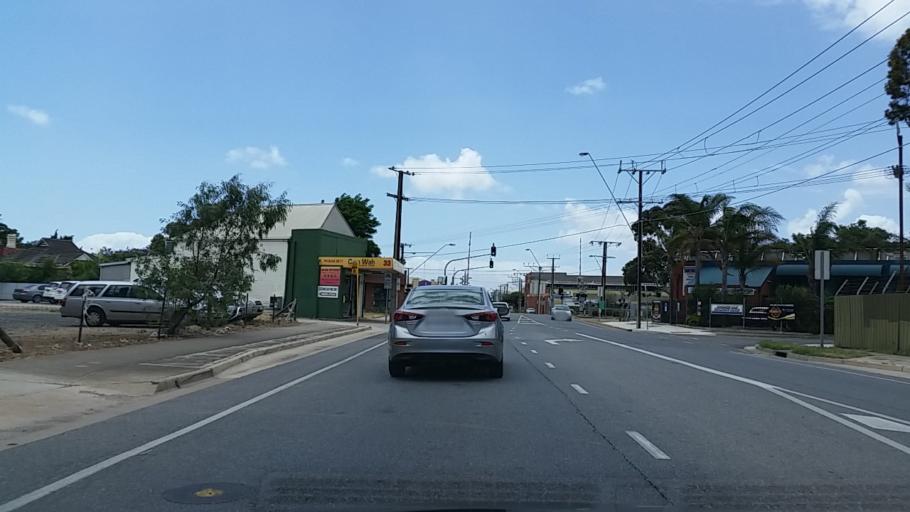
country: AU
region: South Australia
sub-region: Charles Sturt
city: Woodville
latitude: -34.8865
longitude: 138.5488
